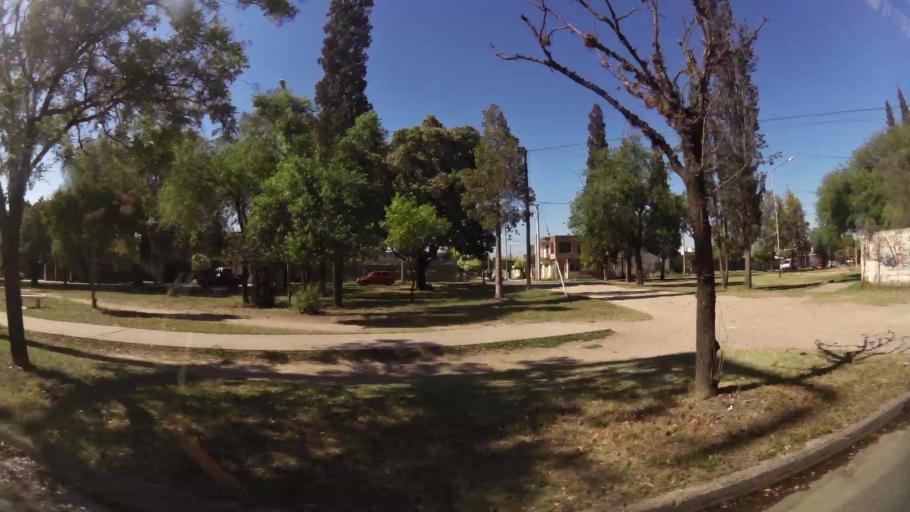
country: AR
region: Cordoba
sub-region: Departamento de Capital
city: Cordoba
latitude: -31.4354
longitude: -64.1404
